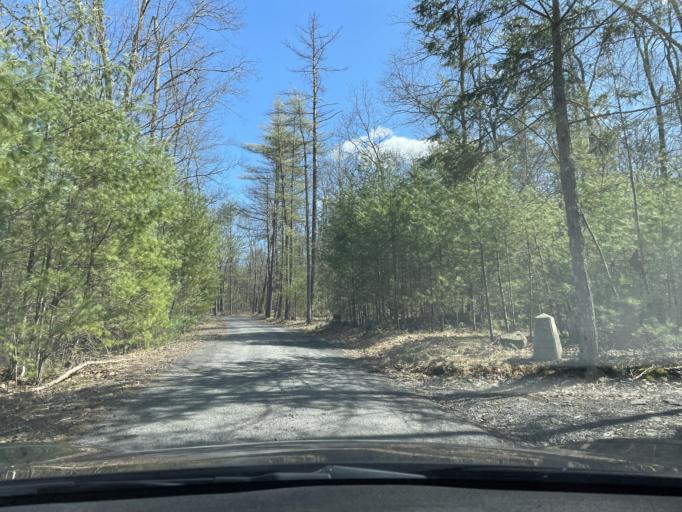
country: US
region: New York
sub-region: Ulster County
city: West Hurley
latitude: 41.9521
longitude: -74.1113
